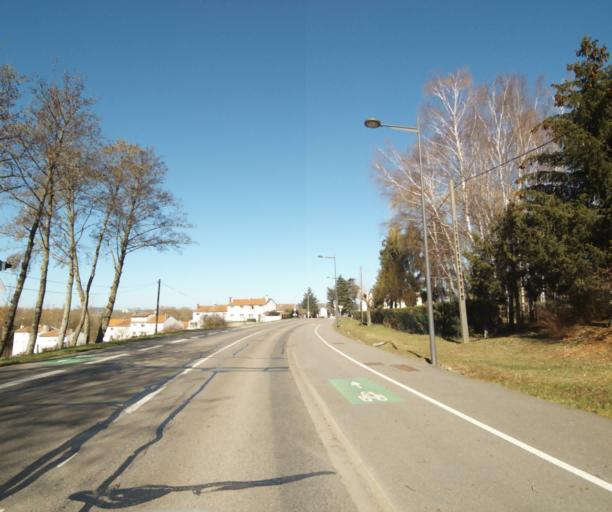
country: FR
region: Lorraine
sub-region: Departement de Meurthe-et-Moselle
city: Heillecourt
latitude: 48.6577
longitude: 6.2064
